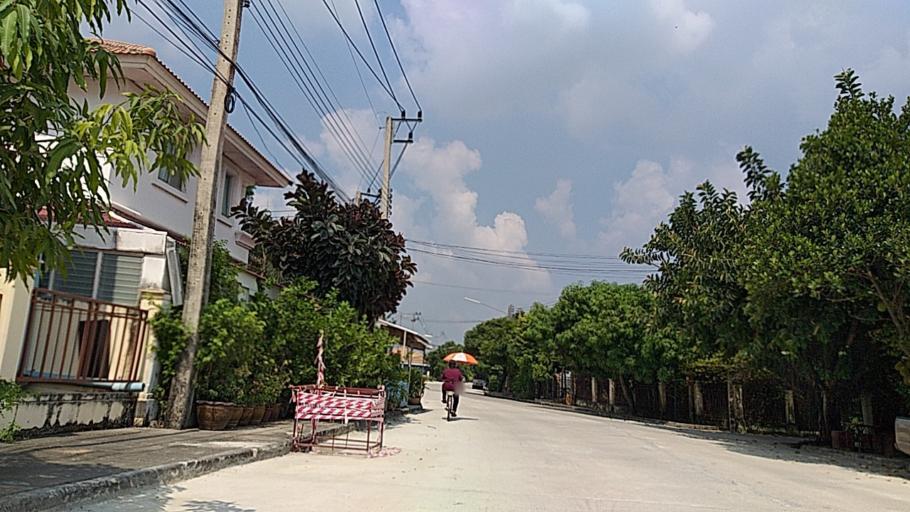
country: TH
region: Pathum Thani
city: Ban Rangsit
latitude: 14.0374
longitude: 100.7654
